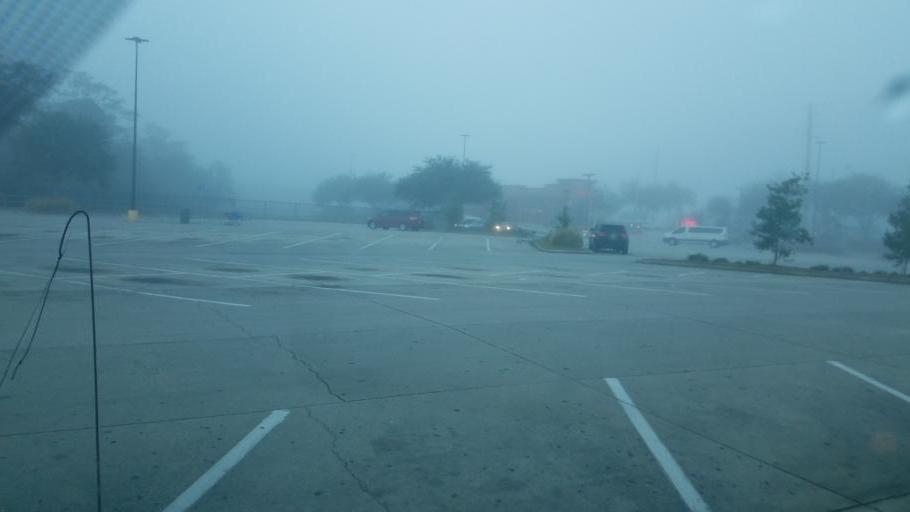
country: US
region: Florida
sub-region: Osceola County
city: Kissimmee
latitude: 28.3029
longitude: -81.4595
